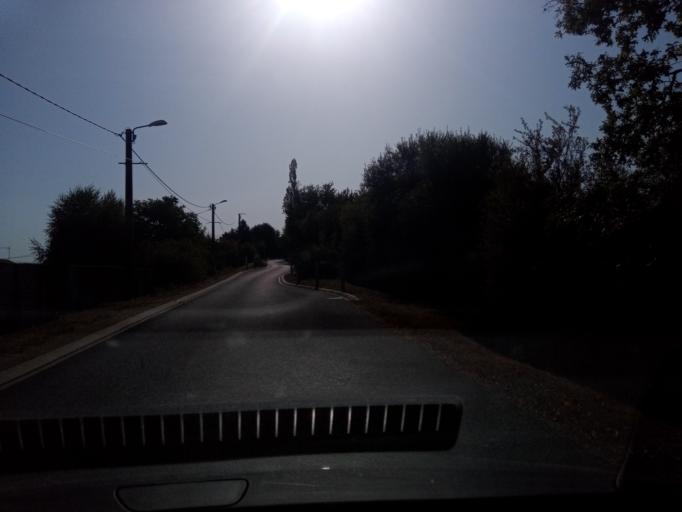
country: FR
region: Poitou-Charentes
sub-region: Departement de la Vienne
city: Saulge
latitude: 46.3746
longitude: 0.8796
